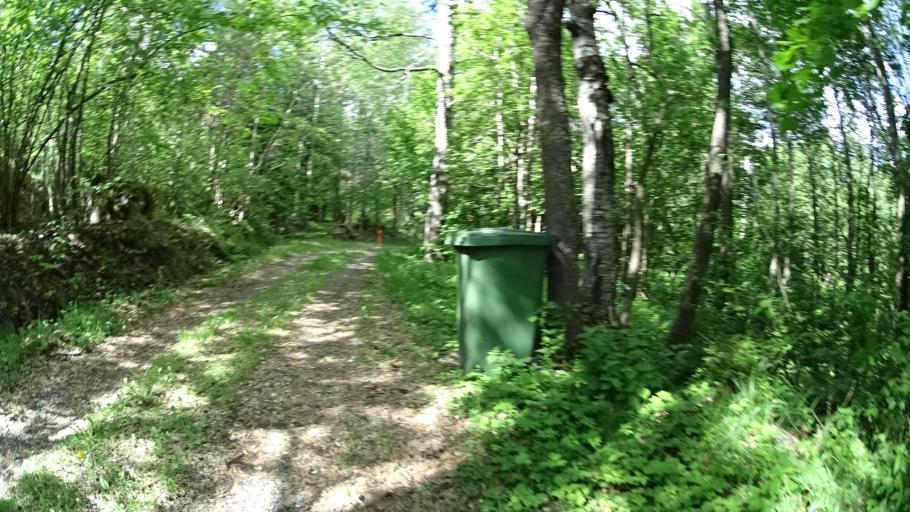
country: FI
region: Uusimaa
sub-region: Raaseporin
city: Pohja
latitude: 60.1720
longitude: 23.5895
